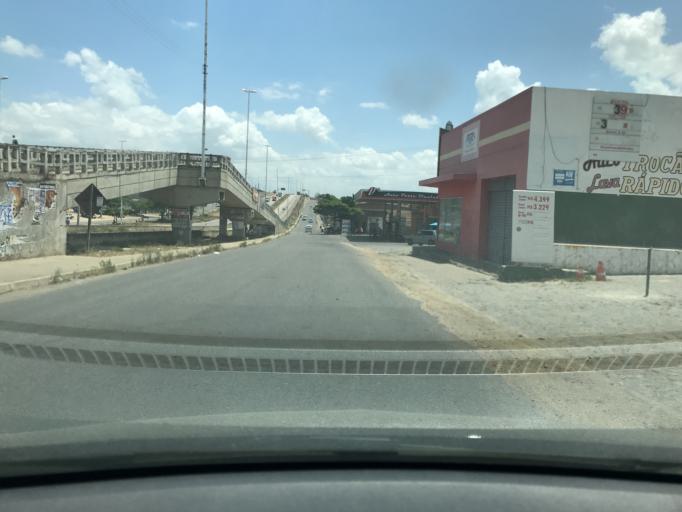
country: BR
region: Pernambuco
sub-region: Bezerros
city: Bezerros
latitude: -8.2441
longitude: -35.7543
